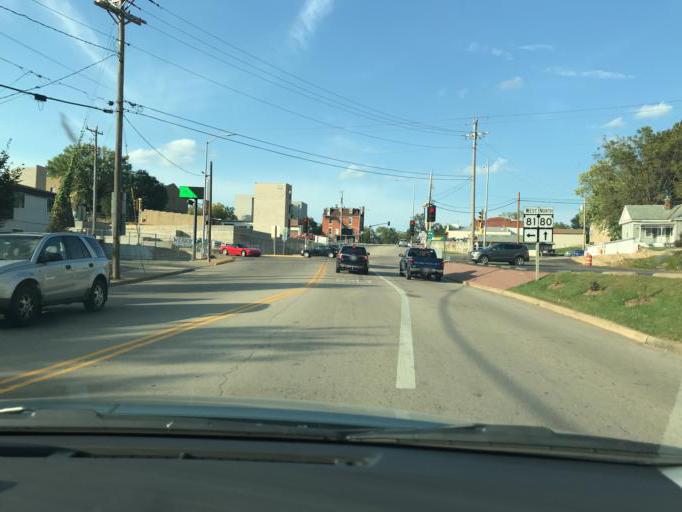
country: US
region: Wisconsin
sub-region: Grant County
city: Platteville
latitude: 42.7318
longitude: -90.4756
